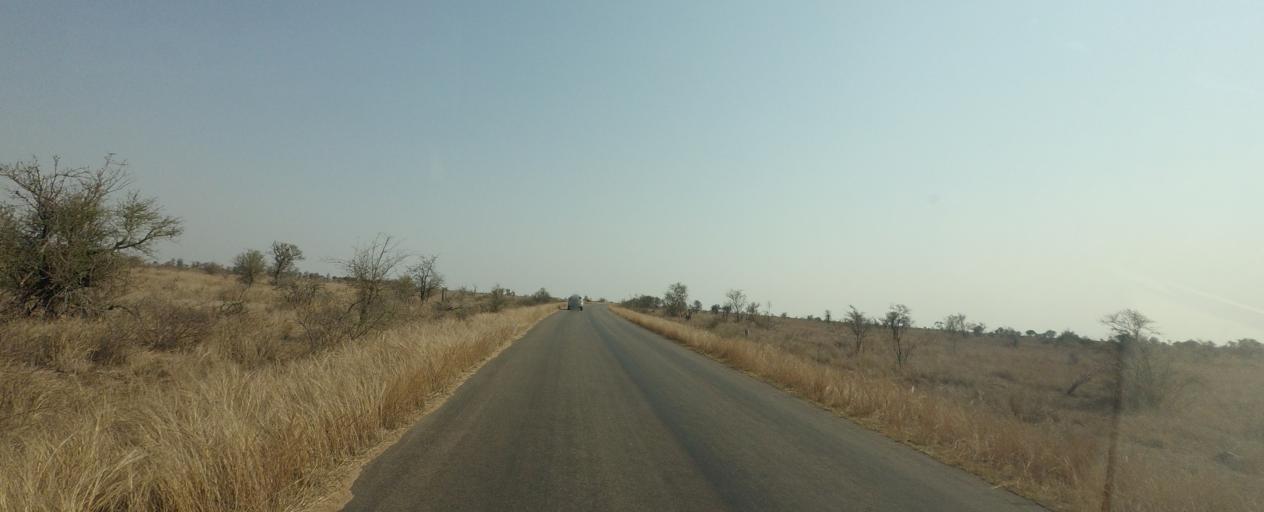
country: ZA
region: Limpopo
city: Thulamahashi
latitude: -24.3625
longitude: 31.7635
